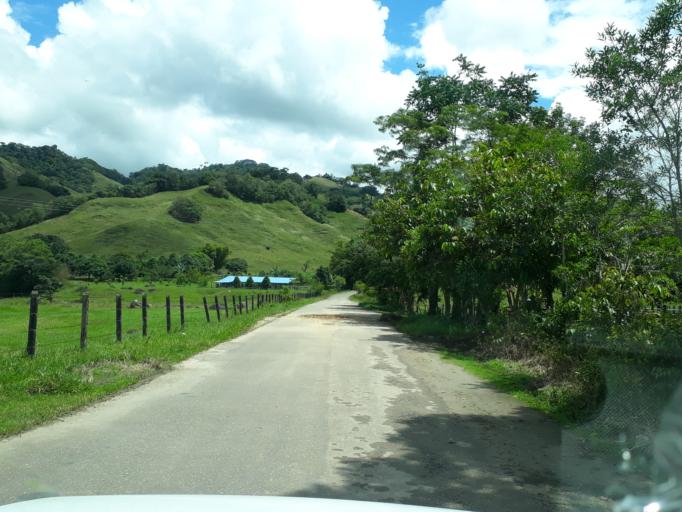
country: CO
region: Cundinamarca
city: Medina
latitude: 4.5813
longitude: -73.3318
